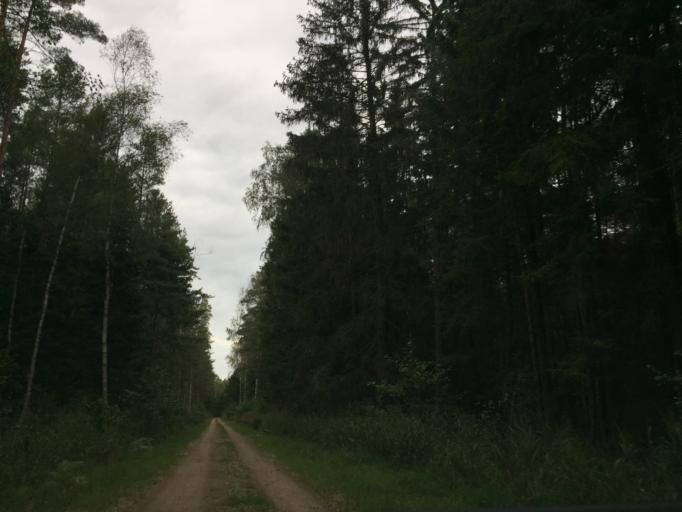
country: LV
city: Tireli
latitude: 56.8890
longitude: 23.5453
